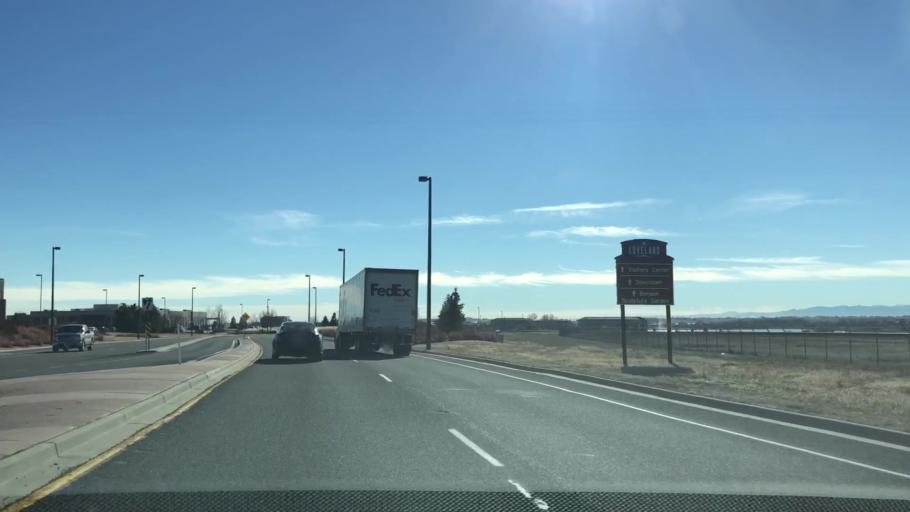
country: US
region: Colorado
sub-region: Larimer County
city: Loveland
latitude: 40.4266
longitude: -105.0004
